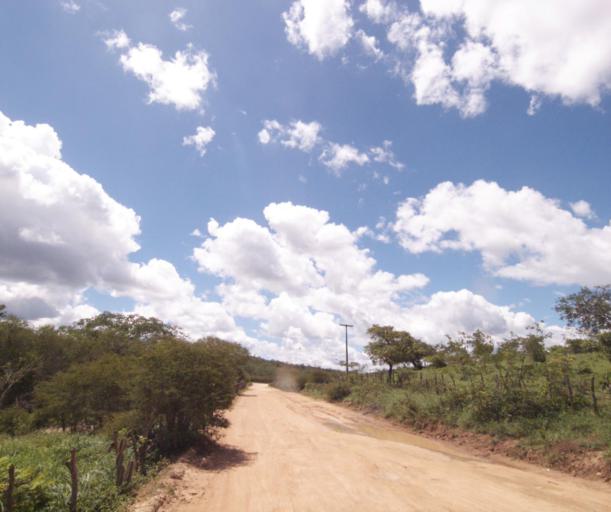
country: BR
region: Bahia
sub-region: Pocoes
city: Pocoes
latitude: -14.3793
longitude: -40.5642
